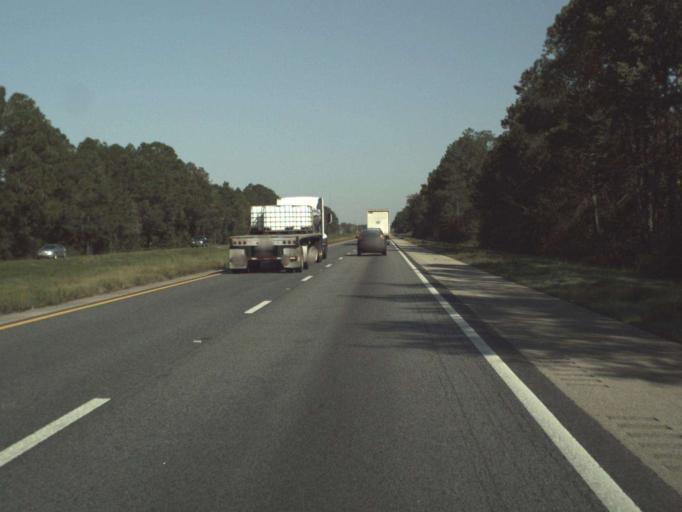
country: US
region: Florida
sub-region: Washington County
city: Chipley
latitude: 30.7457
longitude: -85.4435
